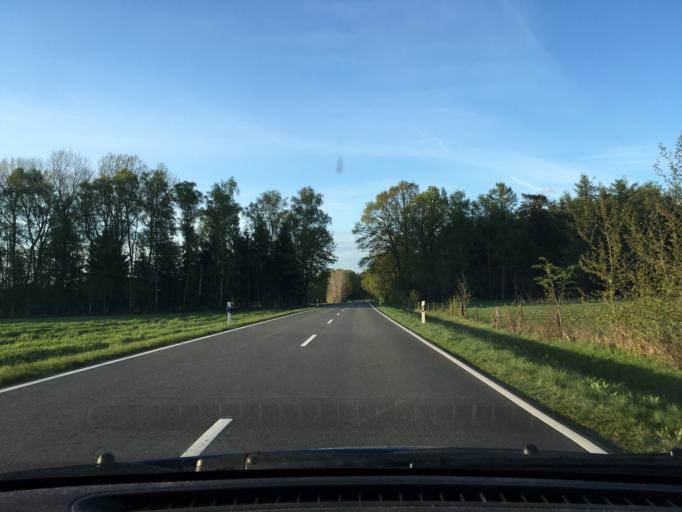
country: DE
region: Lower Saxony
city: Bispingen
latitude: 53.0082
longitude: 9.9970
